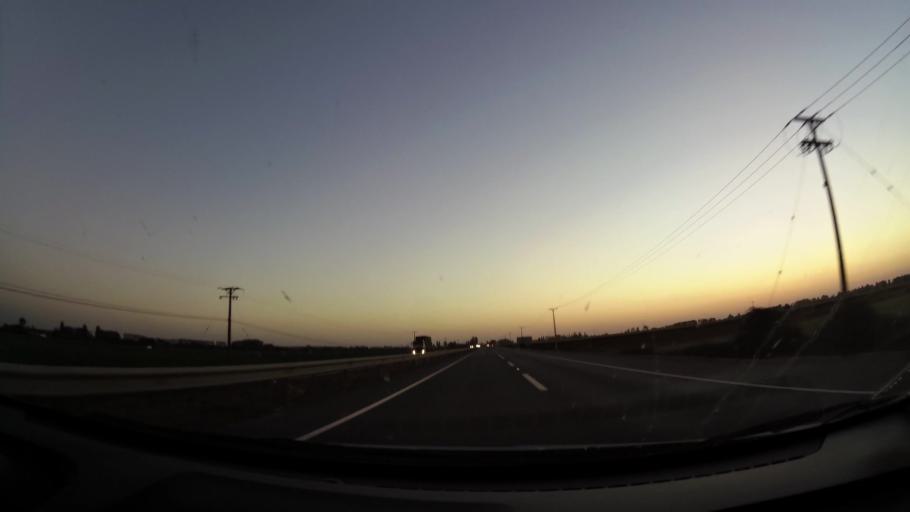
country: CL
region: Maule
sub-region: Provincia de Linares
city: Parral
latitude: -36.0583
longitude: -71.7754
